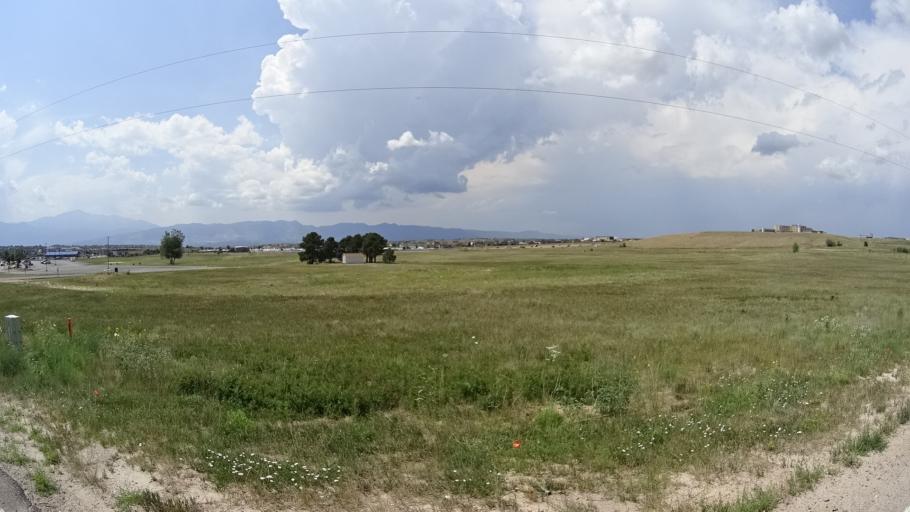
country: US
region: Colorado
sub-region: El Paso County
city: Cimarron Hills
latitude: 38.9287
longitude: -104.7144
